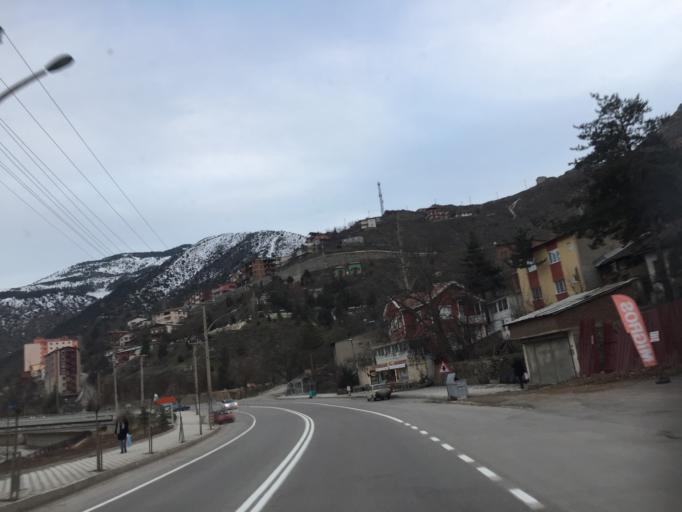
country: TR
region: Gumushane
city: Gumushkhane
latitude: 40.4667
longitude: 39.4634
